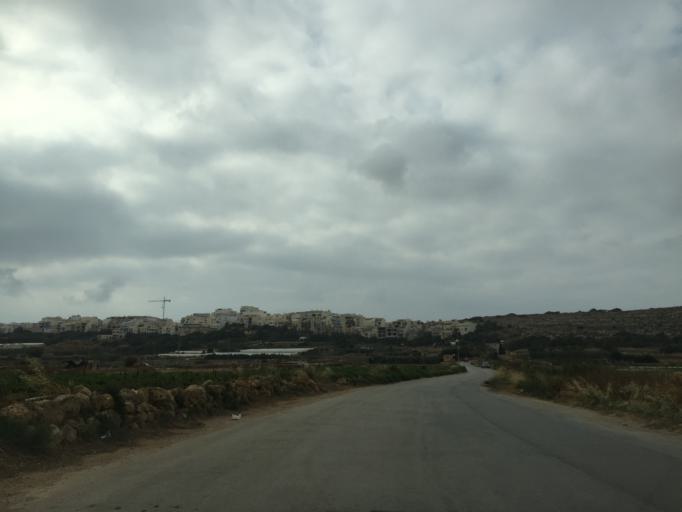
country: MT
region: L-Imgarr
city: Imgarr
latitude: 35.9357
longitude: 14.3586
